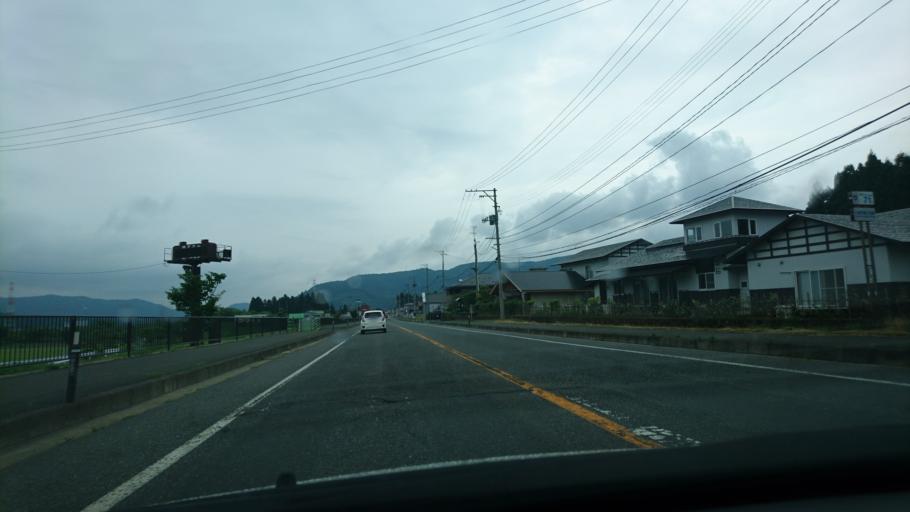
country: JP
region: Miyagi
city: Furukawa
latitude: 38.7385
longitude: 140.7435
